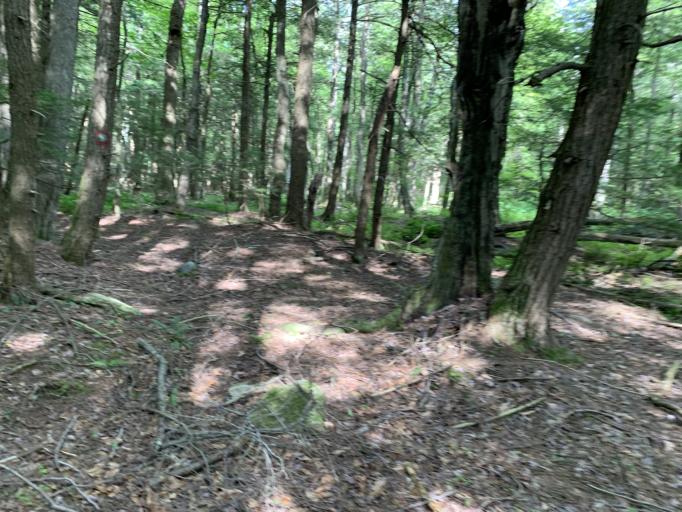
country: US
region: Massachusetts
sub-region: Berkshire County
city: Becket
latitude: 42.2962
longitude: -73.0622
